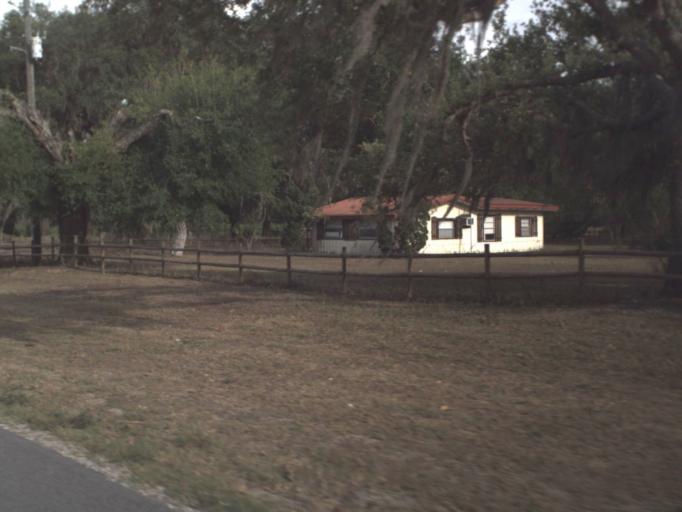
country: US
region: Florida
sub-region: Lake County
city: Mascotte
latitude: 28.5800
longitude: -81.9508
